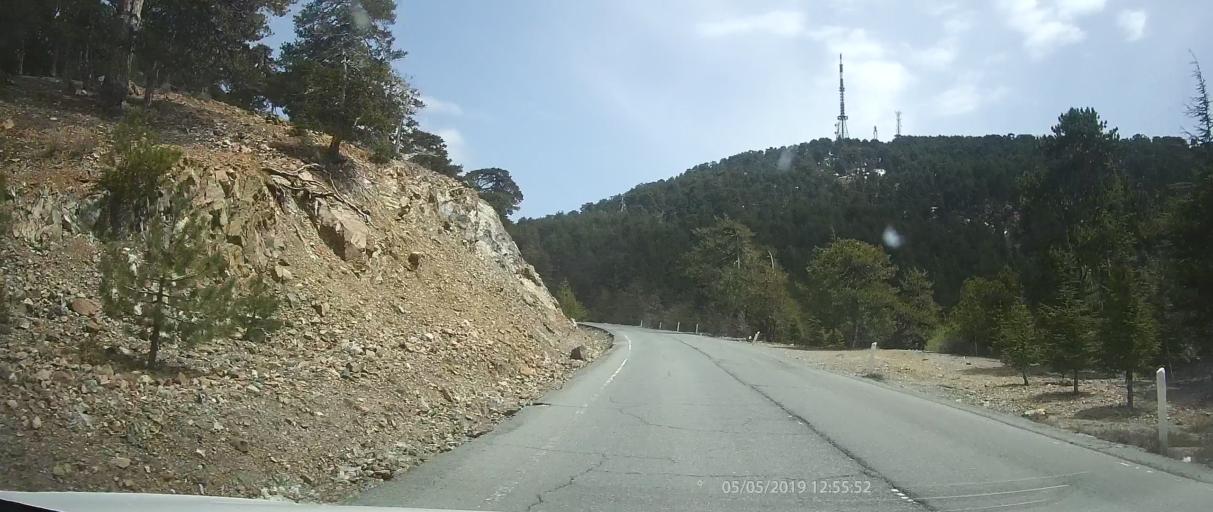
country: CY
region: Lefkosia
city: Kakopetria
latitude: 34.9433
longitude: 32.8574
